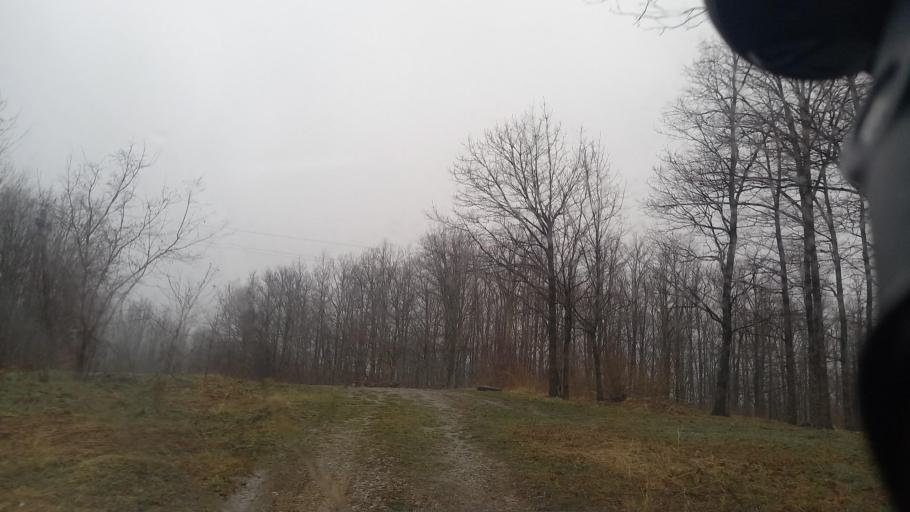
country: RU
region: Krasnodarskiy
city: Saratovskaya
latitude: 44.6150
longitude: 39.2478
